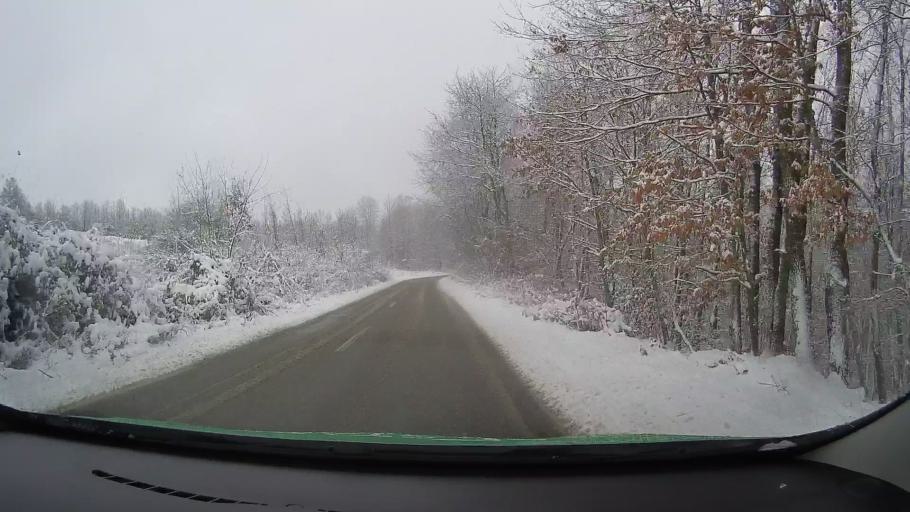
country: RO
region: Hunedoara
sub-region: Comuna Teliucu Inferior
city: Teliucu Inferior
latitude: 45.6813
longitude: 22.9119
